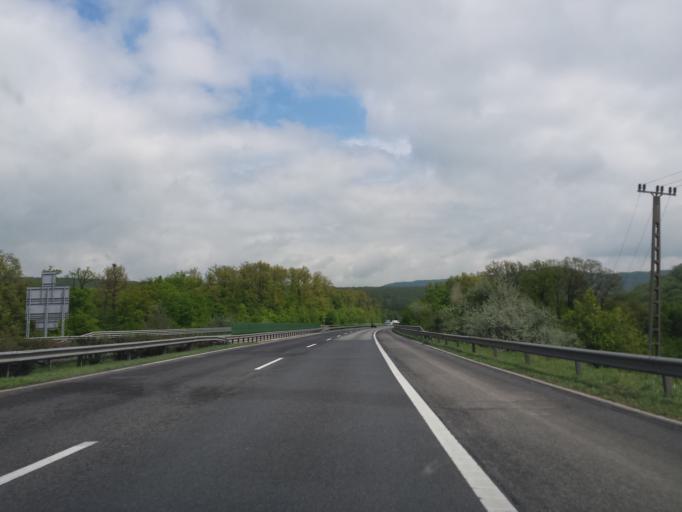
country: HU
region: Komarom-Esztergom
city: Tatabanya
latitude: 47.5757
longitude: 18.4533
